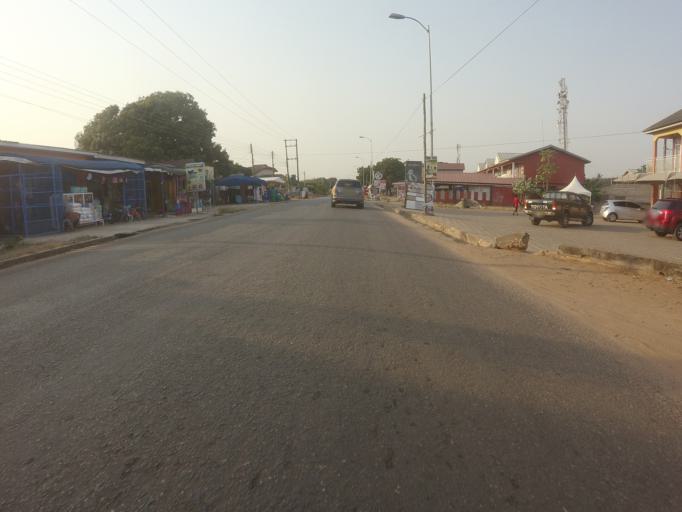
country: GH
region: Greater Accra
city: Nungua
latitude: 5.6204
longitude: -0.0554
